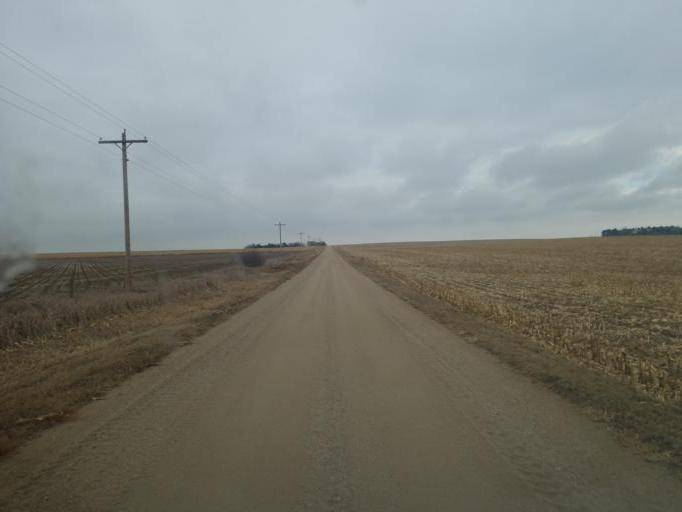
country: US
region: Nebraska
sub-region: Pierce County
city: Plainview
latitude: 42.3798
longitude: -97.7898
